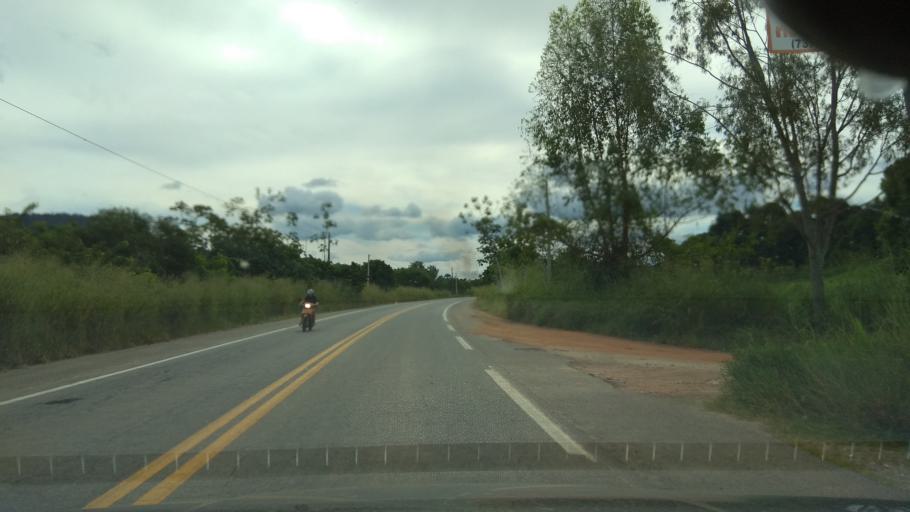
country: BR
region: Bahia
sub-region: Ipiau
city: Ipiau
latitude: -14.1732
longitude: -39.6814
